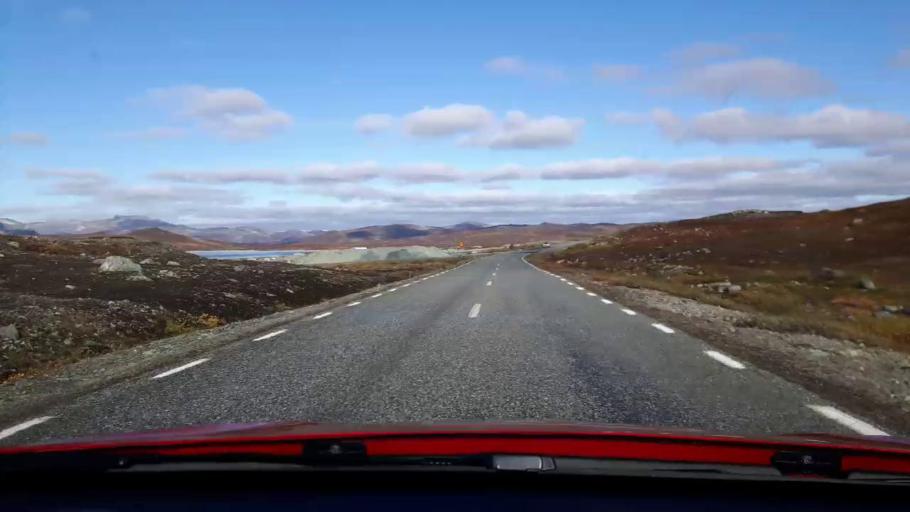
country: NO
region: Nordland
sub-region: Hattfjelldal
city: Hattfjelldal
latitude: 65.0882
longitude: 14.4589
